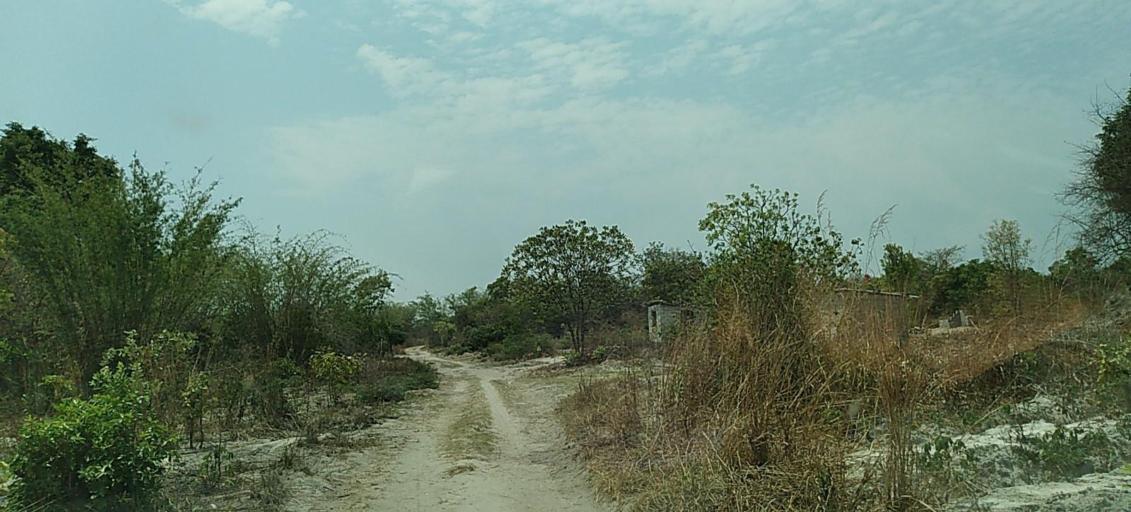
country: ZM
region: Copperbelt
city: Kalulushi
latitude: -12.9427
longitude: 28.1214
